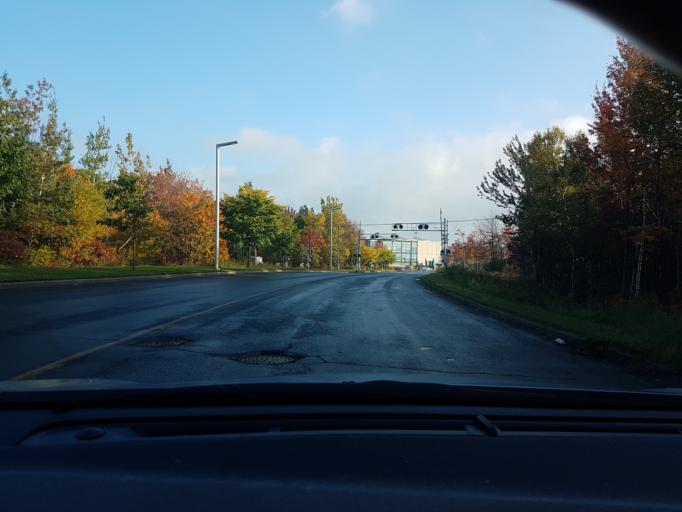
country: CA
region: Quebec
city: L'Ancienne-Lorette
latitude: 46.7982
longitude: -71.3146
